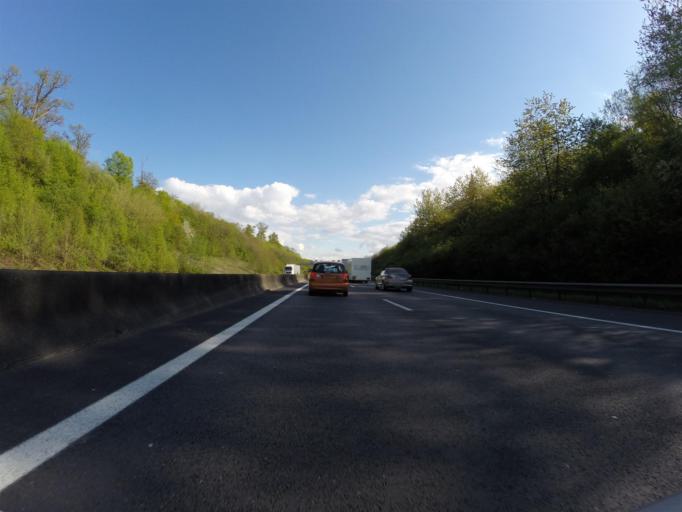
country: LU
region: Luxembourg
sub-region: Canton de Luxembourg
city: Hesperange
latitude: 49.5649
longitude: 6.1288
